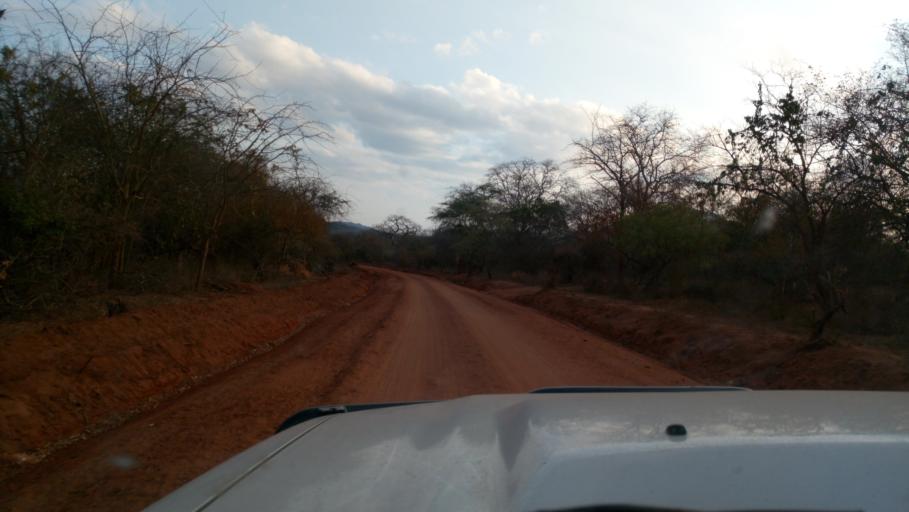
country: KE
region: Kitui
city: Kitui
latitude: -1.6422
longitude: 38.2631
